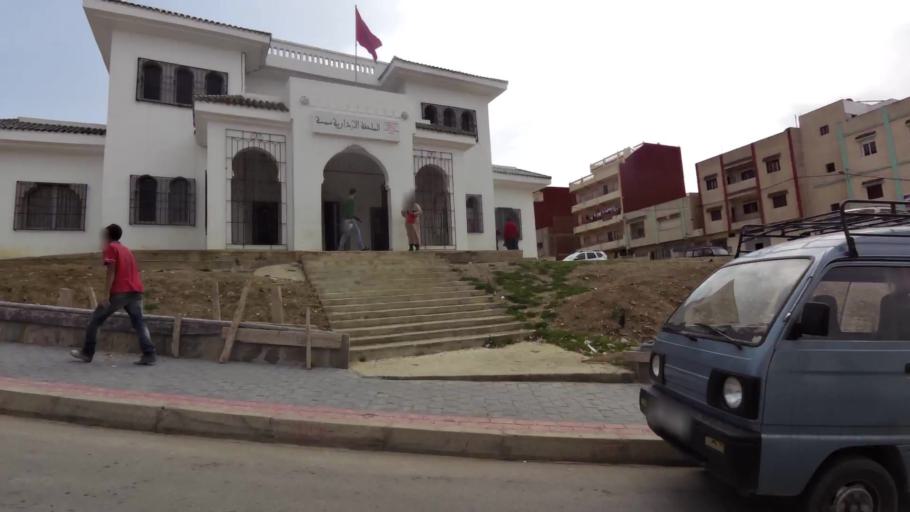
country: MA
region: Tanger-Tetouan
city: Tetouan
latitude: 35.5734
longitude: -5.3963
